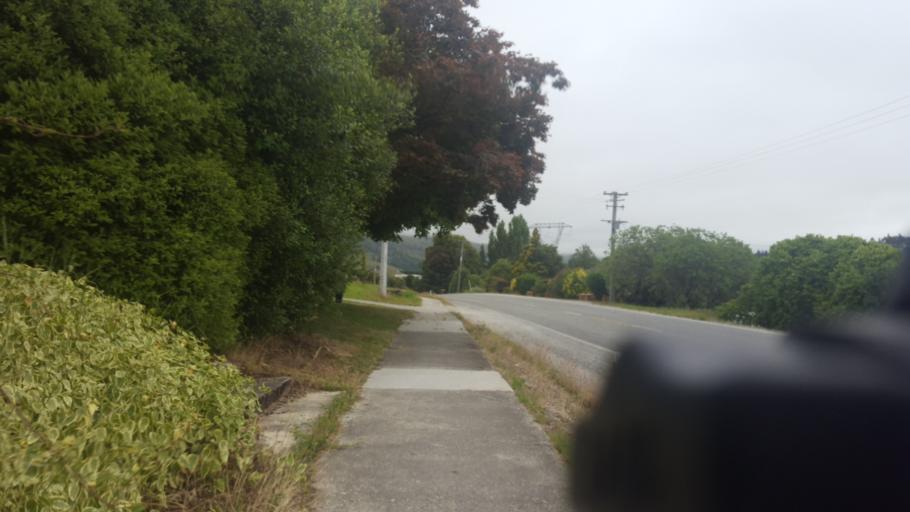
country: NZ
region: Otago
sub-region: Queenstown-Lakes District
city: Kingston
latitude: -45.5309
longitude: 169.2987
